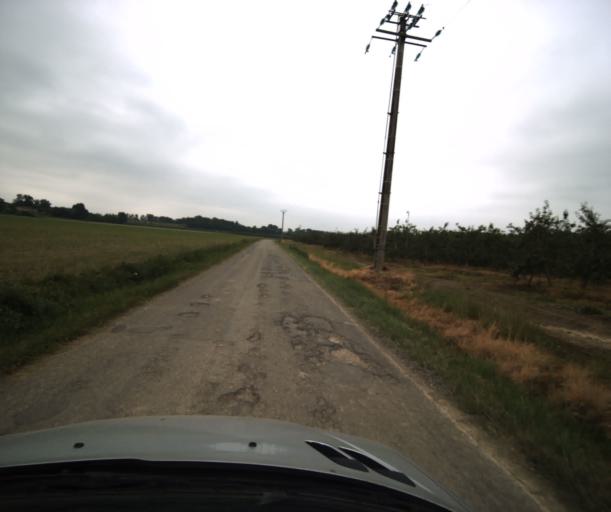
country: FR
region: Midi-Pyrenees
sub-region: Departement du Tarn-et-Garonne
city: Saint-Nicolas-de-la-Grave
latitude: 44.0694
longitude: 0.9872
